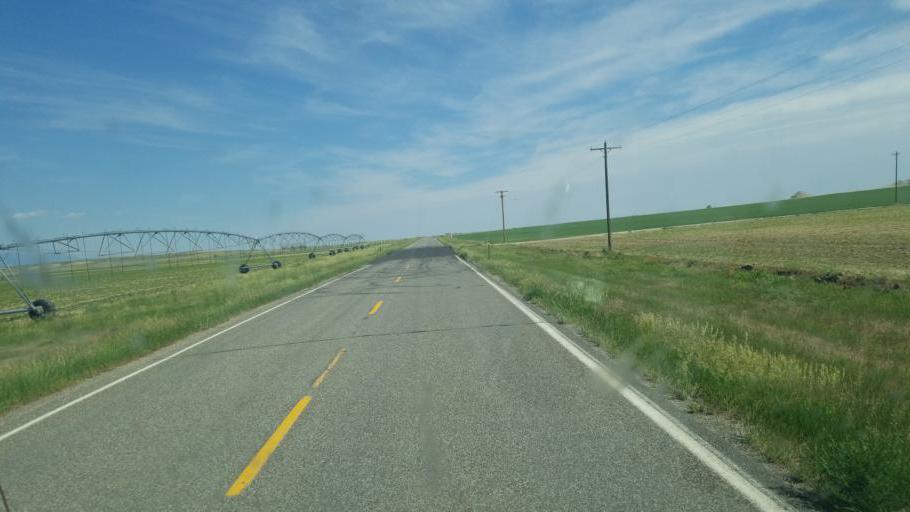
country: US
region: Wyoming
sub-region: Park County
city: Powell
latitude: 44.7756
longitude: -108.9330
